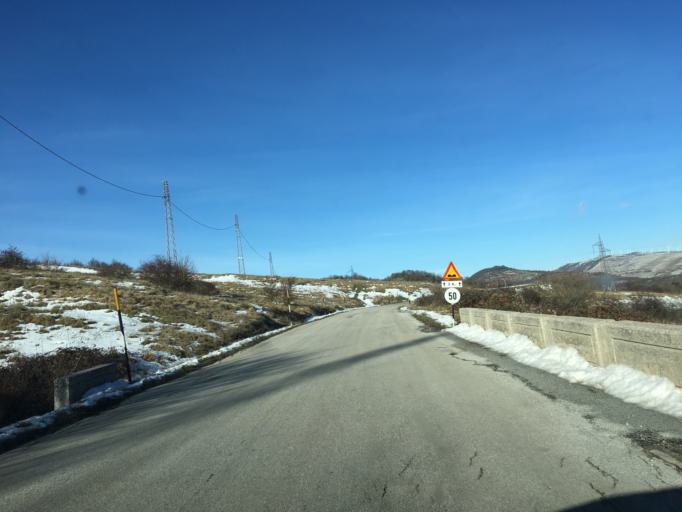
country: IT
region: Abruzzo
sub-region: Provincia di Chieti
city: Rosello
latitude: 41.8578
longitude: 14.3563
